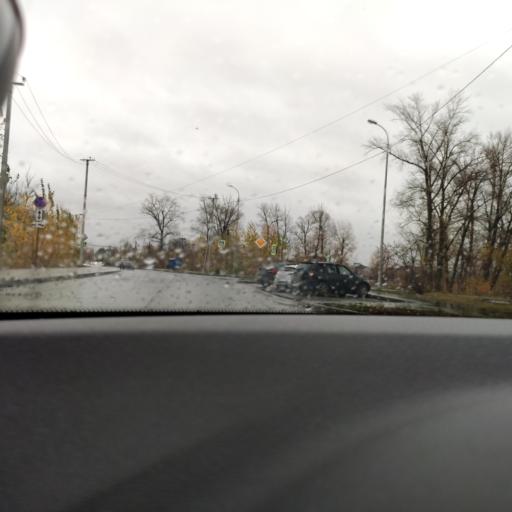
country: RU
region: Samara
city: Rozhdestveno
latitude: 53.1575
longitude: 50.0789
